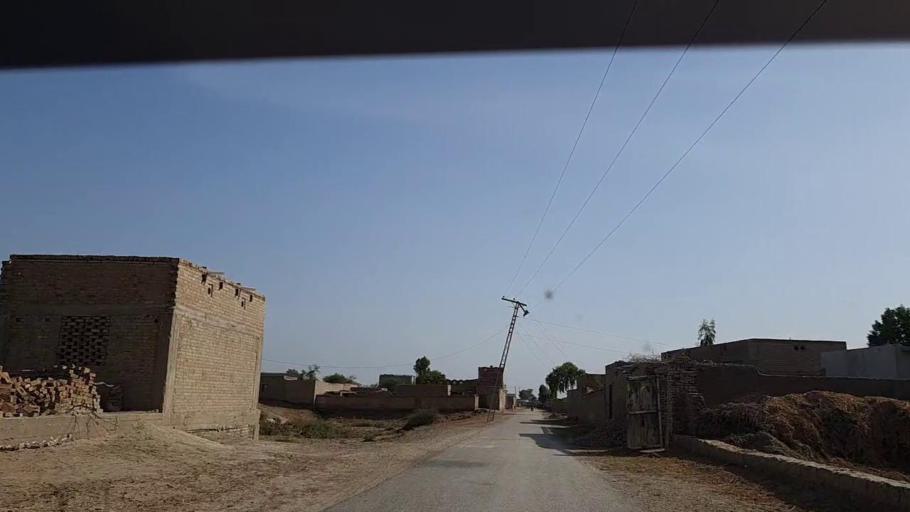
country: PK
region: Sindh
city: Phulji
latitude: 26.9937
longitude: 67.6650
